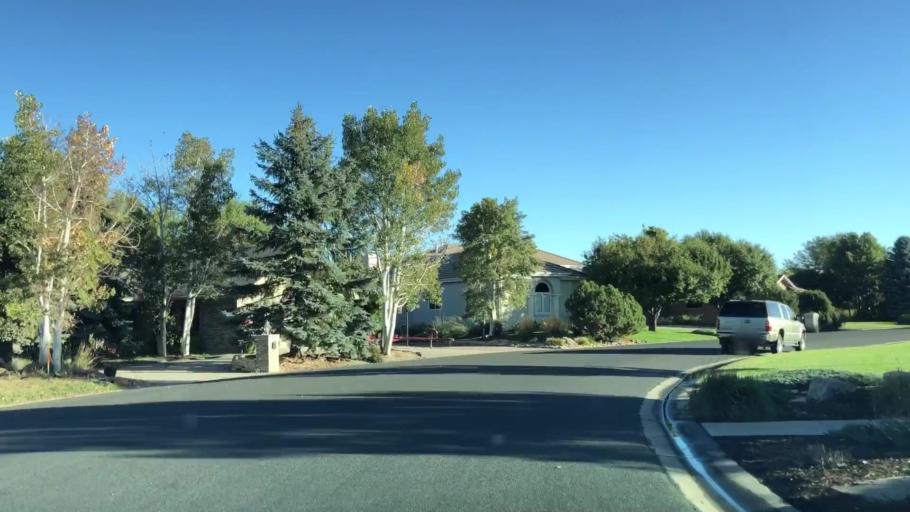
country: US
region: Colorado
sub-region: Larimer County
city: Loveland
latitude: 40.4331
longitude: -105.0249
